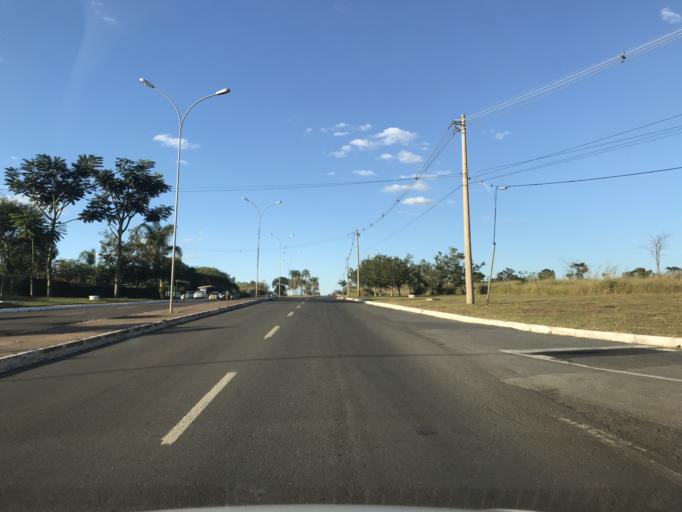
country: BR
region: Federal District
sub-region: Brasilia
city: Brasilia
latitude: -15.8112
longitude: -47.8444
